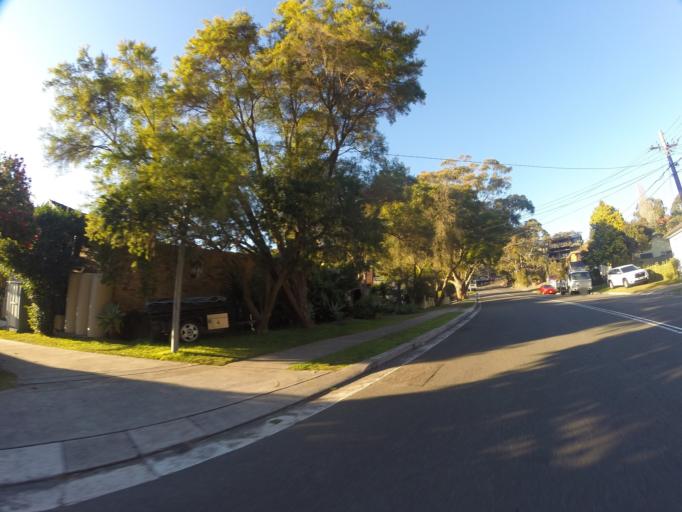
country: AU
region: New South Wales
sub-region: Sutherland Shire
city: Grays Point
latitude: -34.0573
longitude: 151.0760
